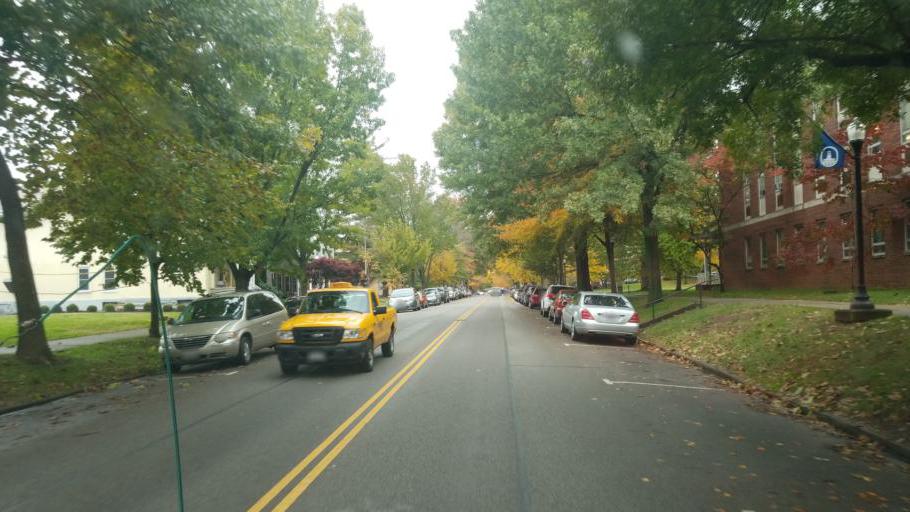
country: US
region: Ohio
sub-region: Washington County
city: Marietta
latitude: 39.4157
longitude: -81.4507
